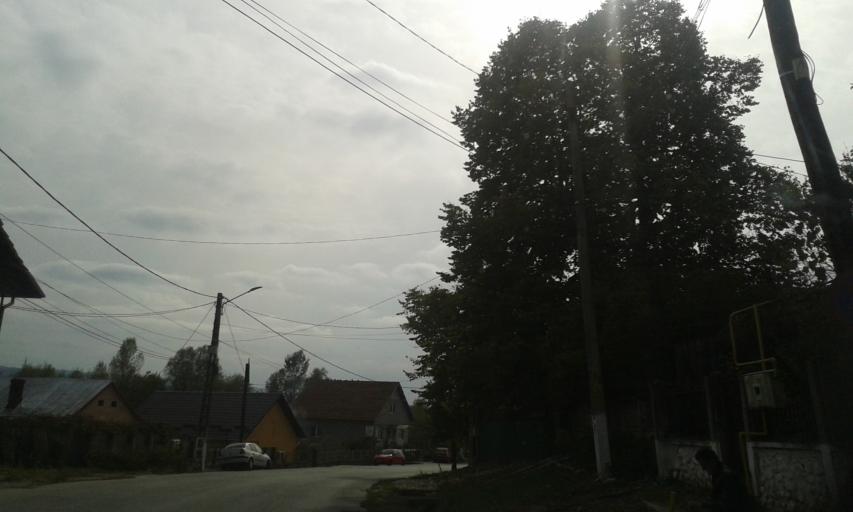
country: RO
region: Gorj
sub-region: Comuna Targu Carbunesti
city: Targu Carbunesti
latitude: 44.9515
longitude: 23.5139
